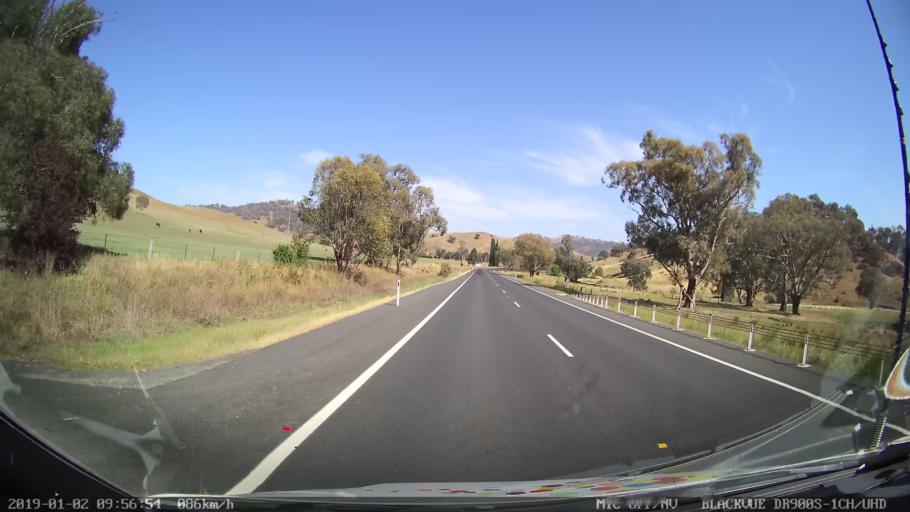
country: AU
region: New South Wales
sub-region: Tumut Shire
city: Tumut
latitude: -35.2112
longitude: 148.1713
